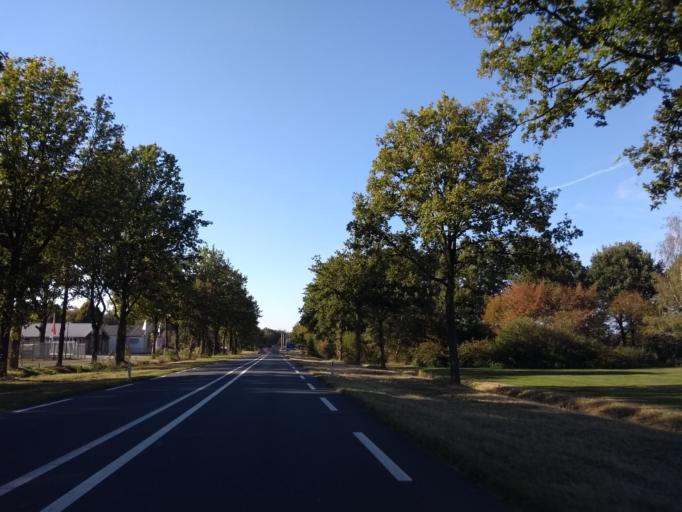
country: NL
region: Overijssel
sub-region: Gemeente Borne
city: Borne
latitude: 52.3087
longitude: 6.7459
